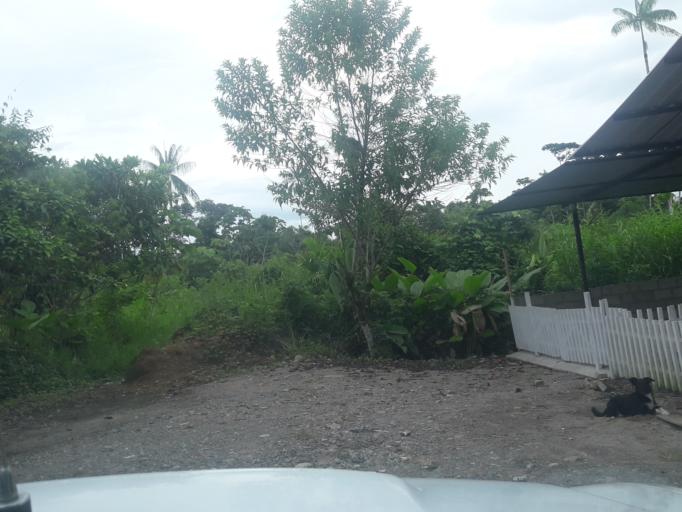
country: EC
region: Napo
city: Tena
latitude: -0.9523
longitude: -77.8136
